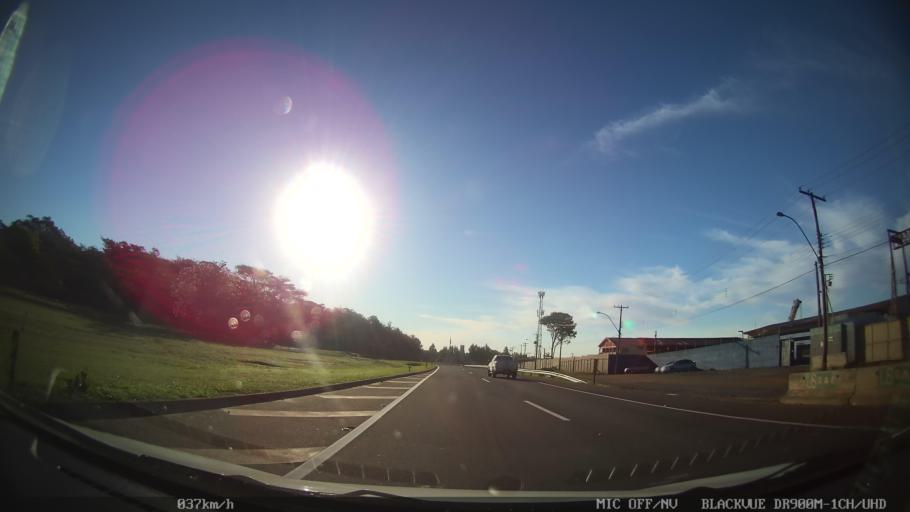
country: BR
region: Sao Paulo
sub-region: Americo Brasiliense
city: Americo Brasiliense
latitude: -21.7467
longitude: -48.1274
